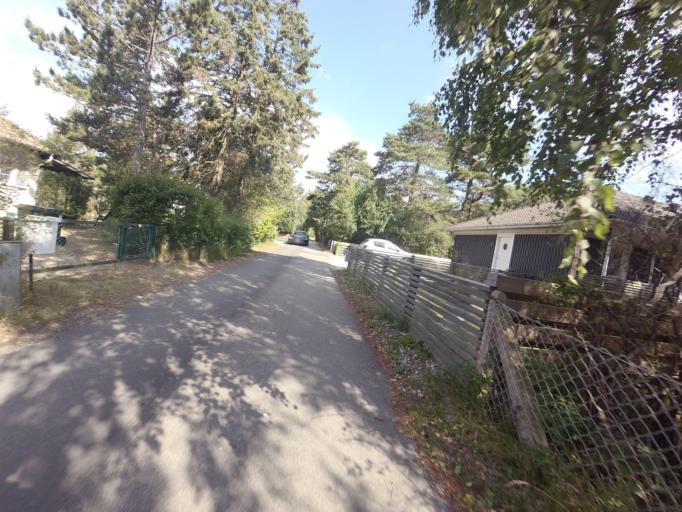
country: SE
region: Skane
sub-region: Vellinge Kommun
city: Hollviken
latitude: 55.4061
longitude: 12.9639
